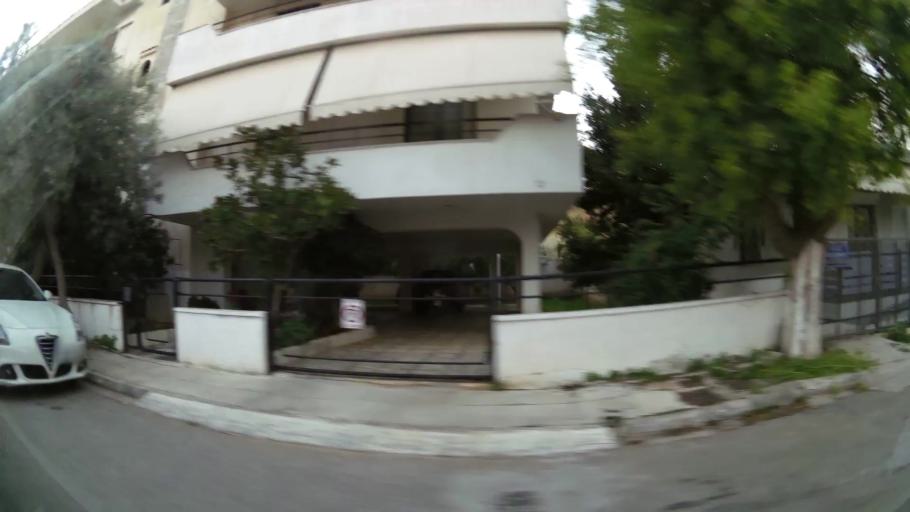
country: GR
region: Attica
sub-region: Nomarchia Athinas
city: Agia Paraskevi
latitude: 38.0198
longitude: 23.8260
